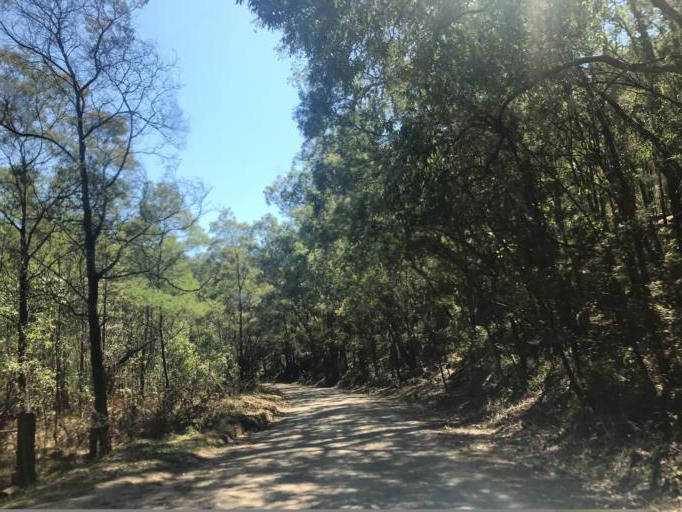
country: AU
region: New South Wales
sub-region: Wyong Shire
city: Little Jilliby
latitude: -33.1970
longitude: 151.0170
